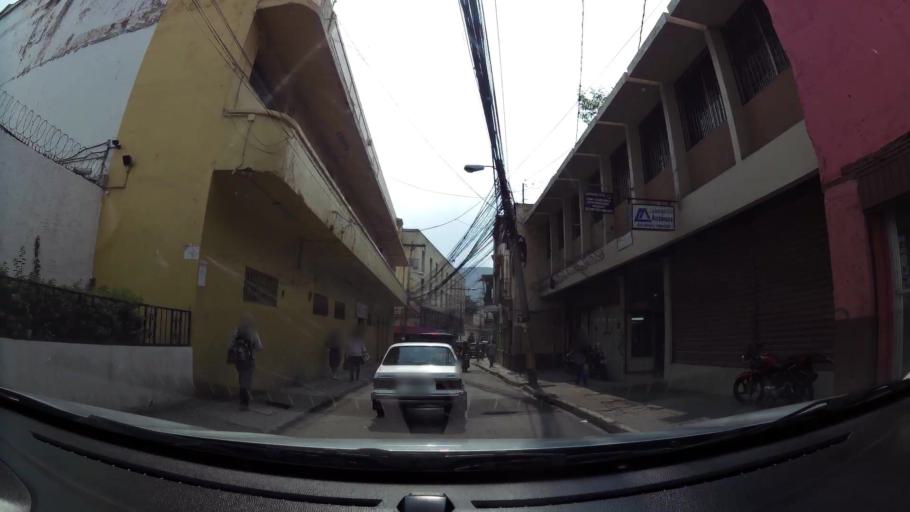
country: HN
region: Francisco Morazan
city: Tegucigalpa
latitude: 14.1071
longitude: -87.2042
